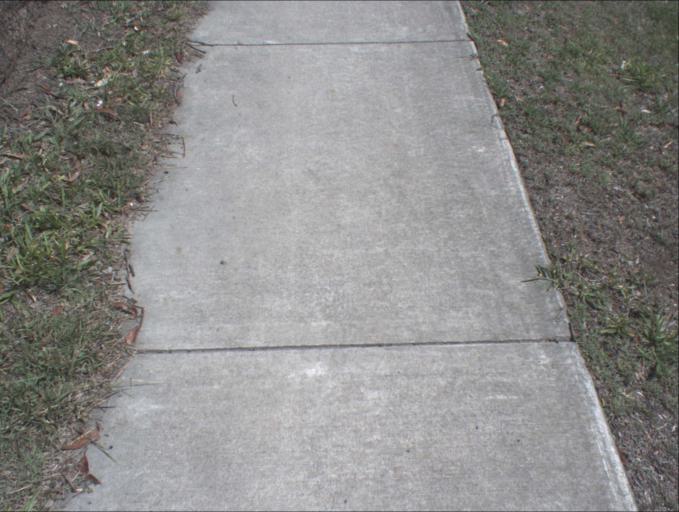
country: AU
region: Queensland
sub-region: Logan
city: Park Ridge South
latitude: -27.7304
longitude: 153.0428
